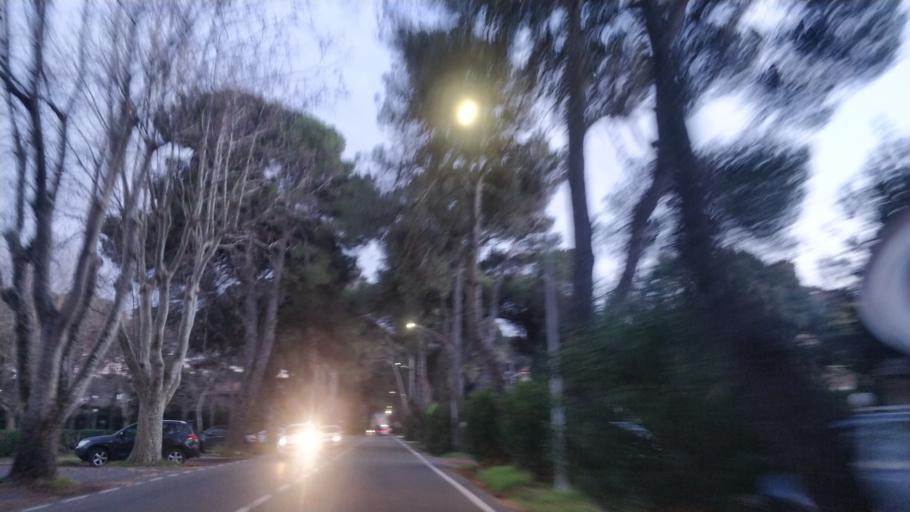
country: IT
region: Tuscany
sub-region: Provincia di Livorno
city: Rosignano Solvay-Castiglioncello
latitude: 43.3905
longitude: 10.4406
